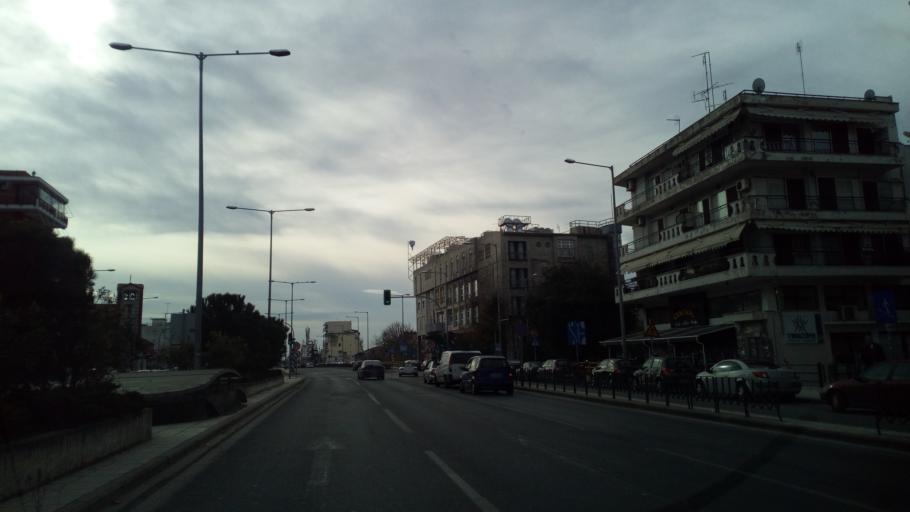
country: GR
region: Central Macedonia
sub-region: Nomos Thessalonikis
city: Stavroupoli
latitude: 40.6657
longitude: 22.9366
